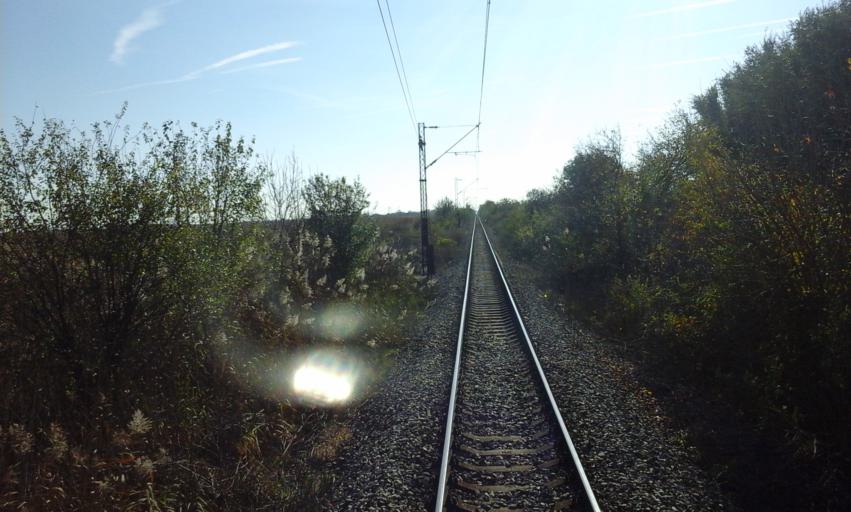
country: RS
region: Autonomna Pokrajina Vojvodina
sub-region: Severnobacki Okrug
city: Subotica
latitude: 46.0566
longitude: 19.6863
